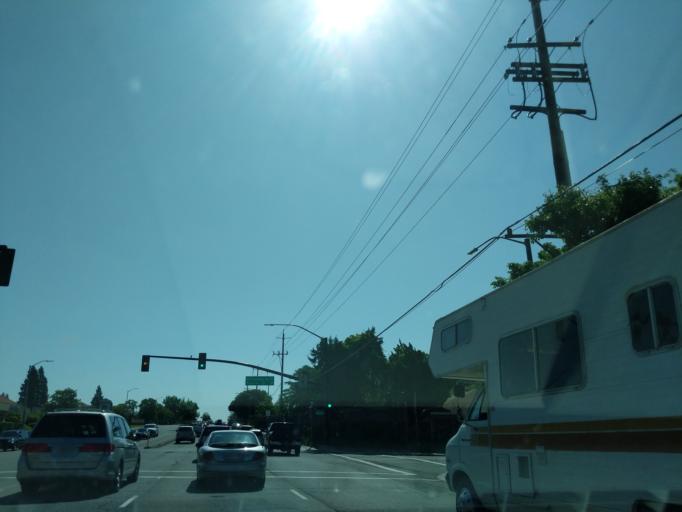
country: US
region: California
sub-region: Sacramento County
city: Citrus Heights
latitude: 38.6782
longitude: -121.2988
